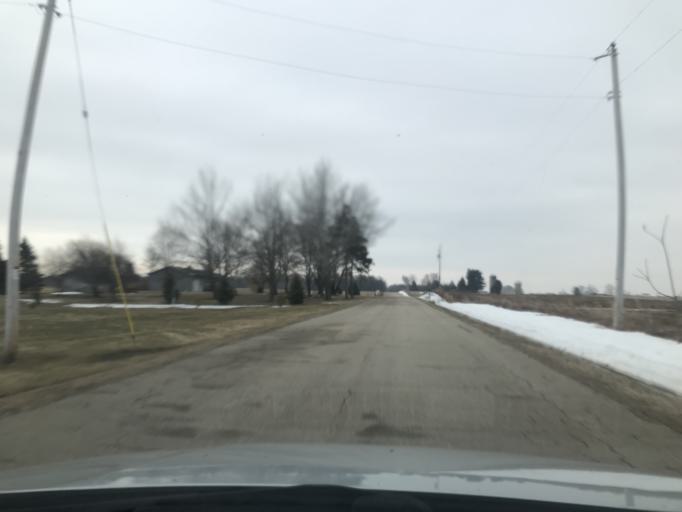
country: US
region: Wisconsin
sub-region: Marinette County
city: Peshtigo
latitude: 45.1250
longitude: -88.0078
